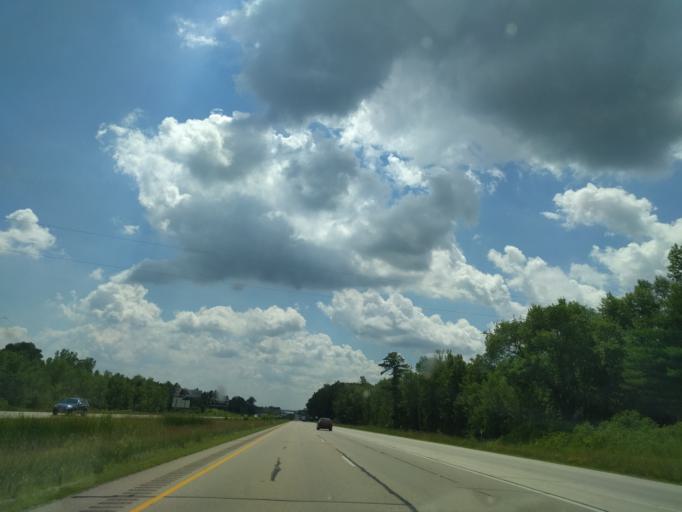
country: US
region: Wisconsin
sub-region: Brown County
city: Suamico
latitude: 44.7176
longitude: -88.0509
